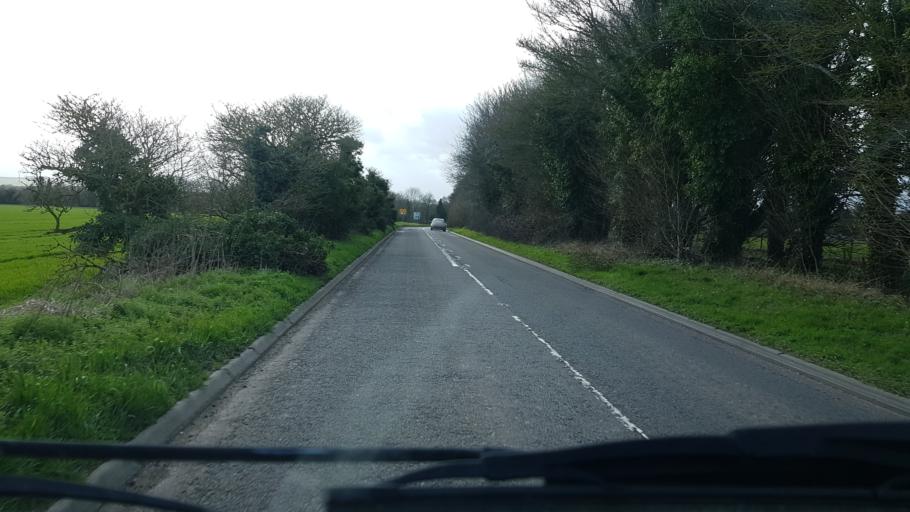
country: GB
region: England
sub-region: Wiltshire
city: Avebury
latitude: 51.4590
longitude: -1.8525
